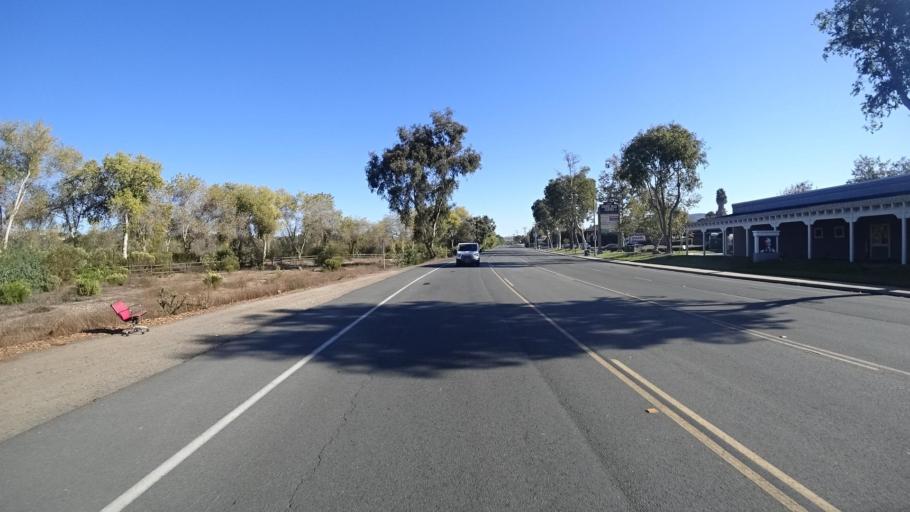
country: US
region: California
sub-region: San Diego County
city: Bonita
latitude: 32.6703
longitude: -117.0223
